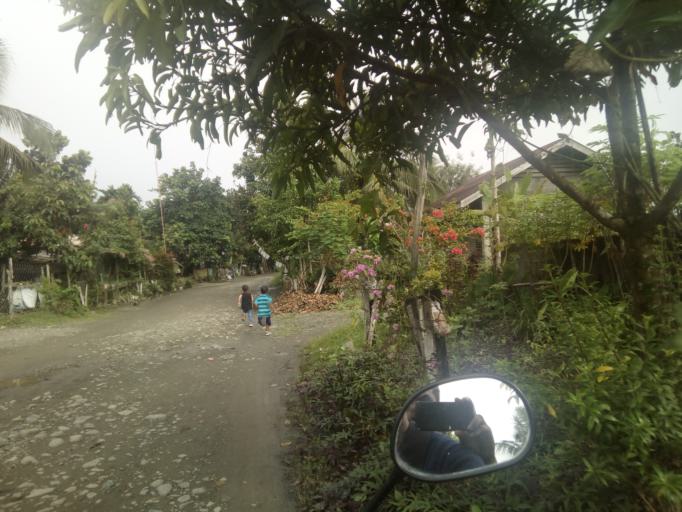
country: PH
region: Caraga
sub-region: Province of Agusan del Sur
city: Santa Josefa
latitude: 8.0211
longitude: 125.9937
